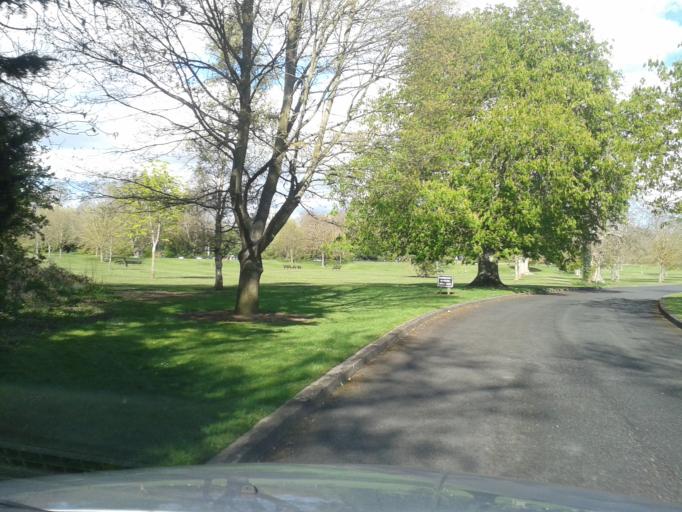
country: IE
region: Leinster
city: Donabate
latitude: 53.4850
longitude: -6.1727
